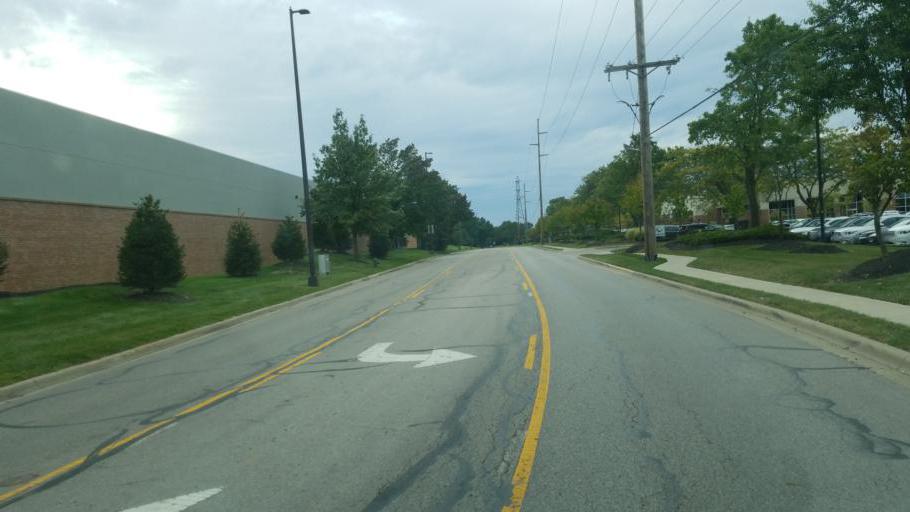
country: US
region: Ohio
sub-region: Franklin County
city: Dublin
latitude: 40.1077
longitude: -83.0932
